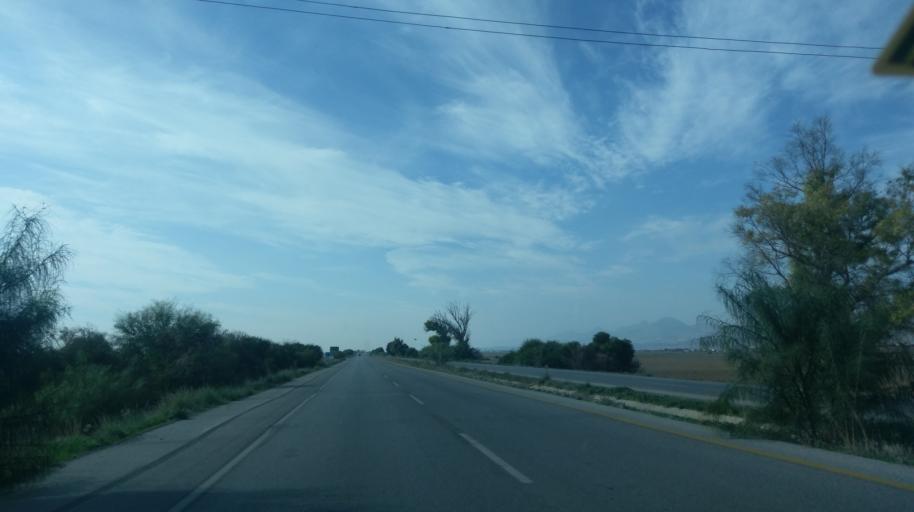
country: CY
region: Larnaka
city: Athienou
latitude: 35.2090
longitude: 33.5785
